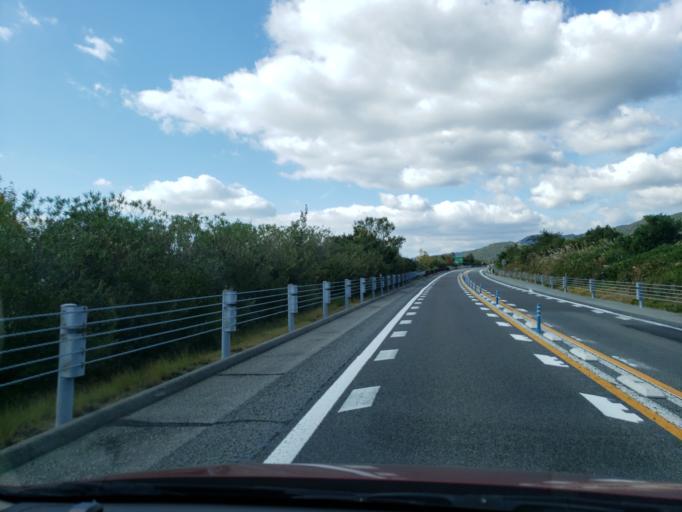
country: JP
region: Tokushima
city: Kamojimacho-jogejima
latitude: 34.1212
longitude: 134.3716
